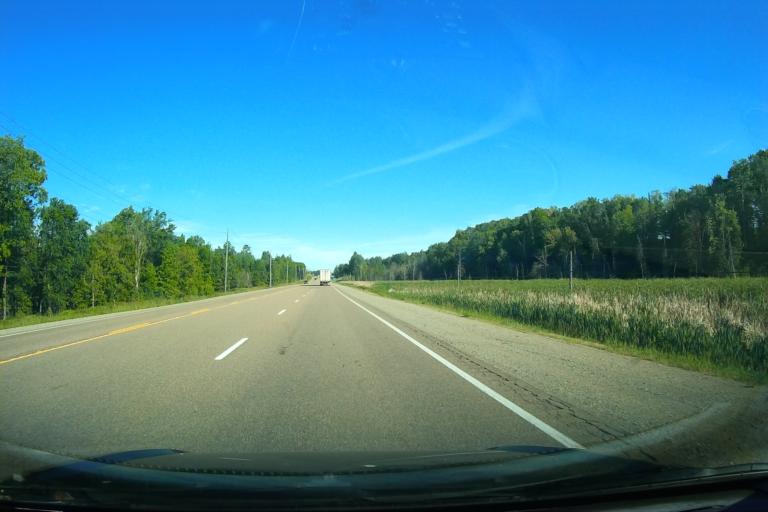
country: CA
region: Ontario
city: Renfrew
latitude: 45.6131
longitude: -76.8609
